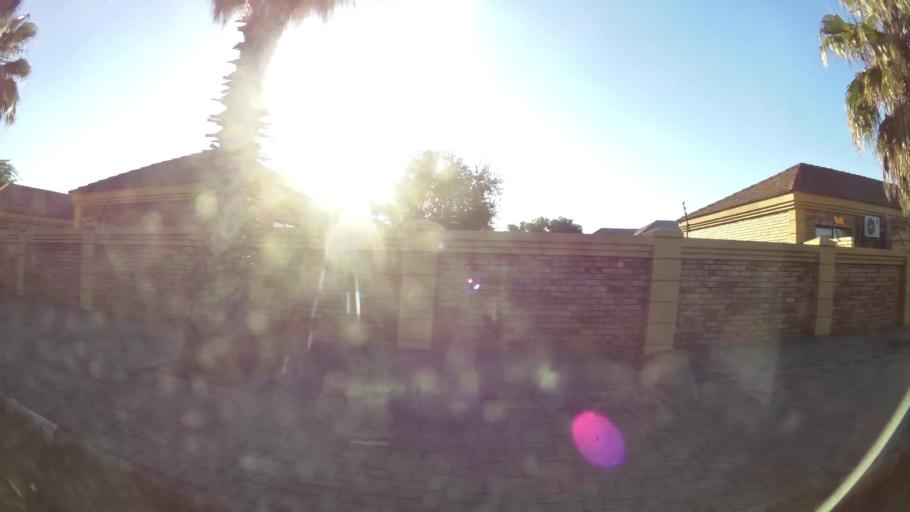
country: ZA
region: Northern Cape
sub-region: Frances Baard District Municipality
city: Kimberley
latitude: -28.7485
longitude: 24.7334
